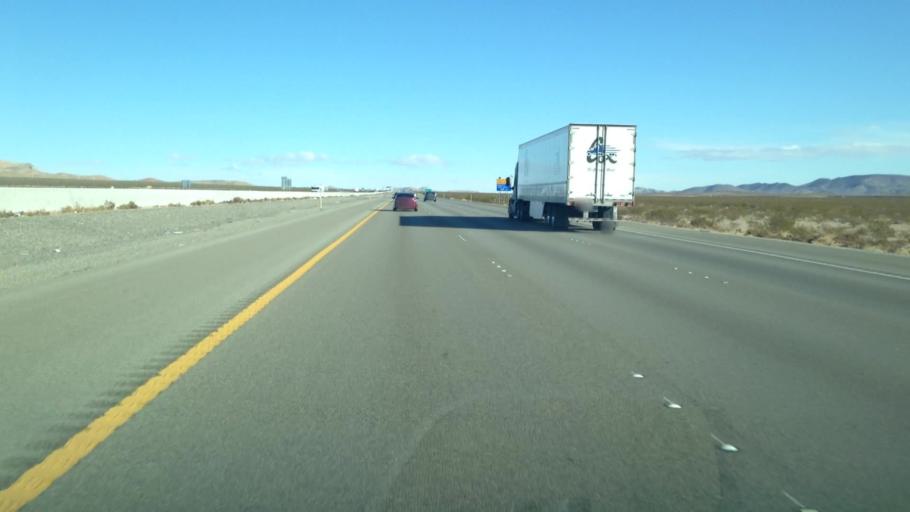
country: US
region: Nevada
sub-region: Clark County
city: Enterprise
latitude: 35.7867
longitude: -115.3235
